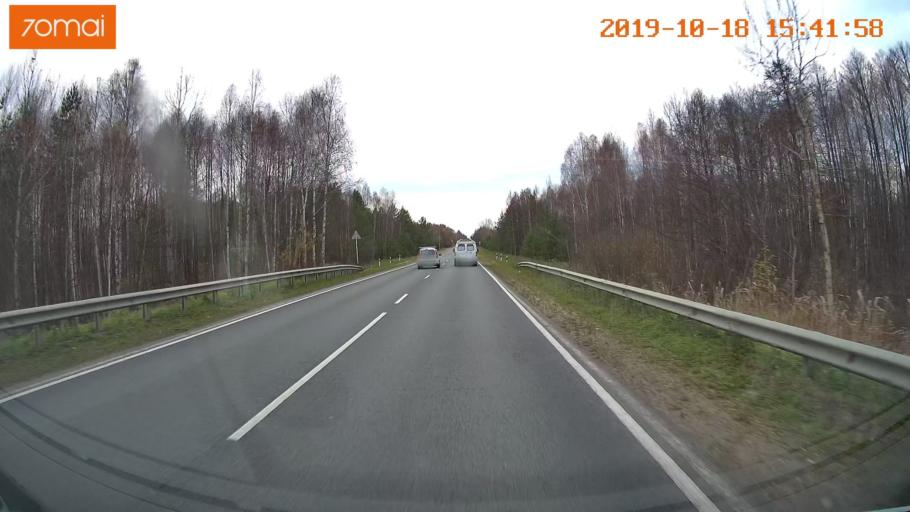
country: RU
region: Vladimir
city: Golovino
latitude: 55.9509
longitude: 40.5749
